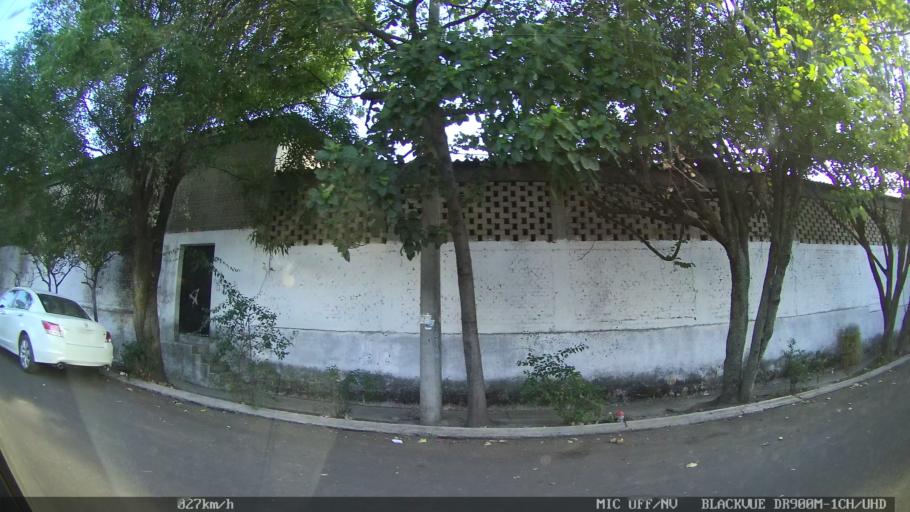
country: MX
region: Jalisco
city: Tlaquepaque
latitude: 20.7093
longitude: -103.3044
